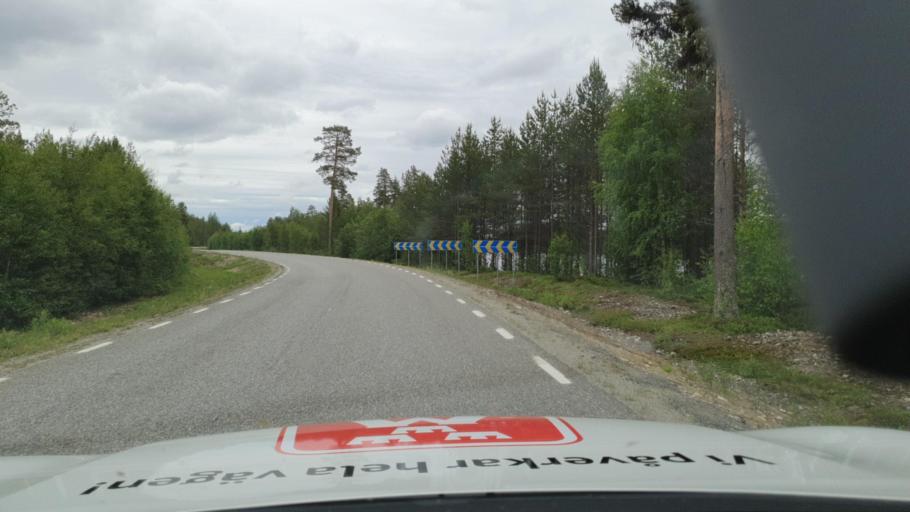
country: SE
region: Vaesterbotten
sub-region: Lycksele Kommun
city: Lycksele
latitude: 64.1754
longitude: 18.3237
